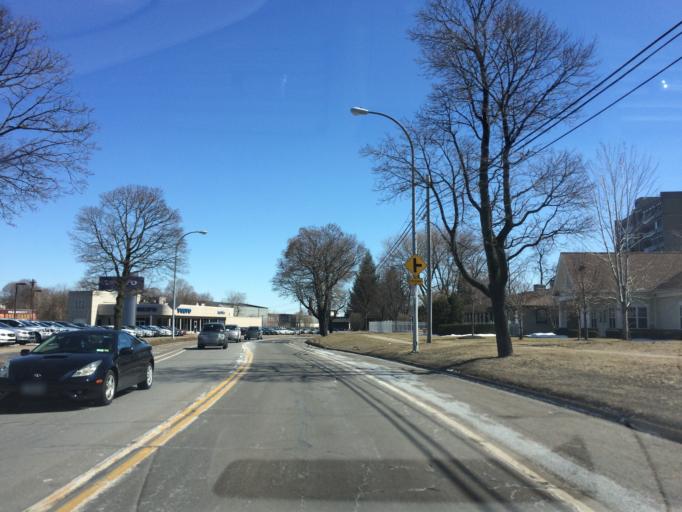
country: US
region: New York
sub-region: Monroe County
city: Brighton
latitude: 43.1491
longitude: -77.5636
